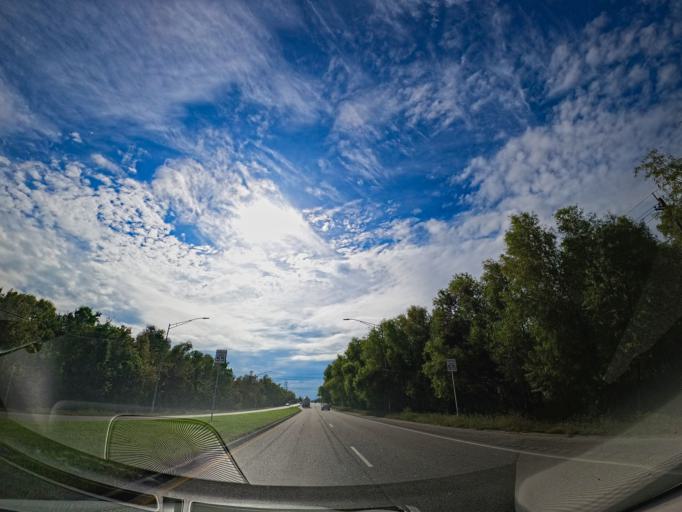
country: US
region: Louisiana
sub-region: Saint Bernard Parish
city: Chalmette
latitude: 30.0392
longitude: -89.9030
